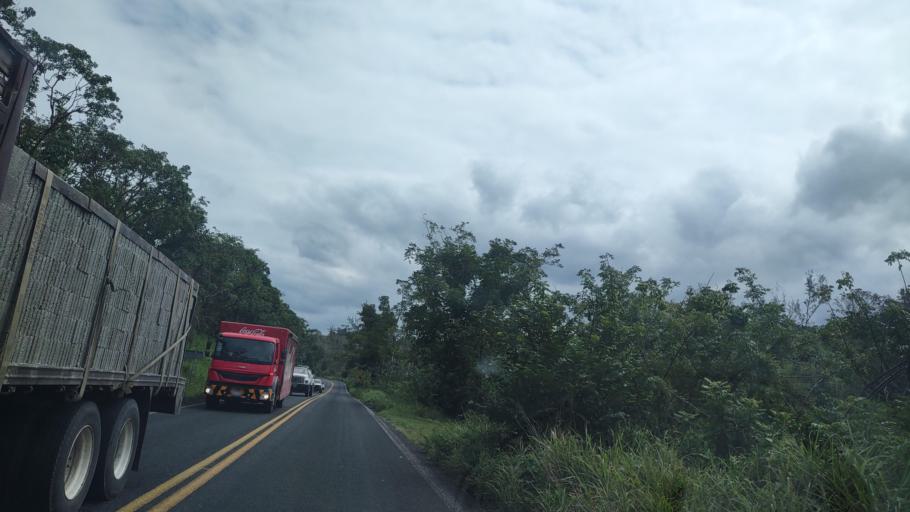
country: MX
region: Veracruz
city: Papantla de Olarte
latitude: 20.4632
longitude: -97.2708
